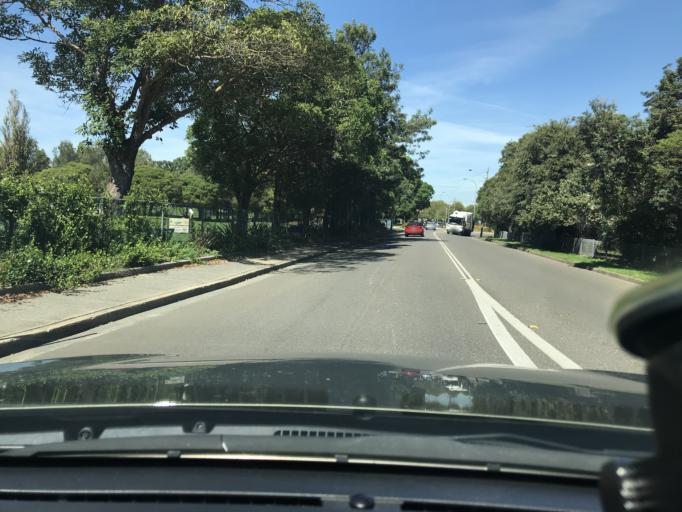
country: AU
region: New South Wales
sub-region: Canada Bay
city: Concord
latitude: -33.8538
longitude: 151.1081
